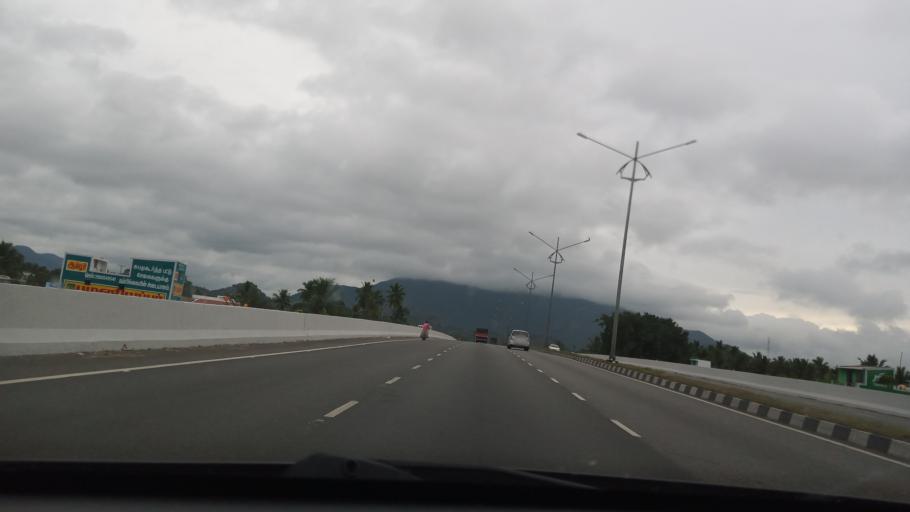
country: IN
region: Tamil Nadu
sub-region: Vellore
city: Ambur
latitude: 12.7477
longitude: 78.6976
